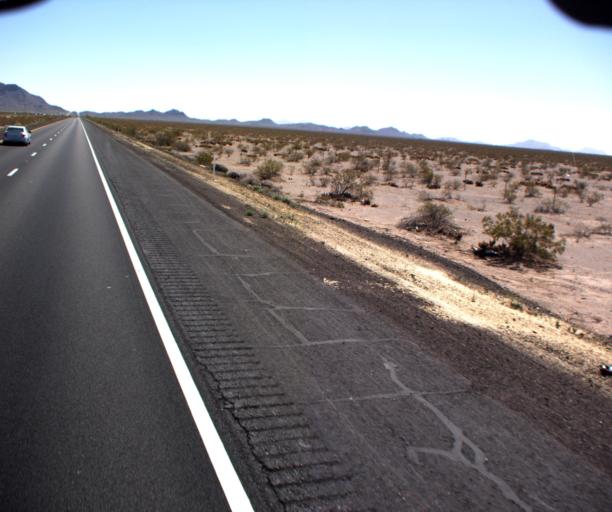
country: US
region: Arizona
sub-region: La Paz County
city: Salome
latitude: 33.6199
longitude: -113.6948
